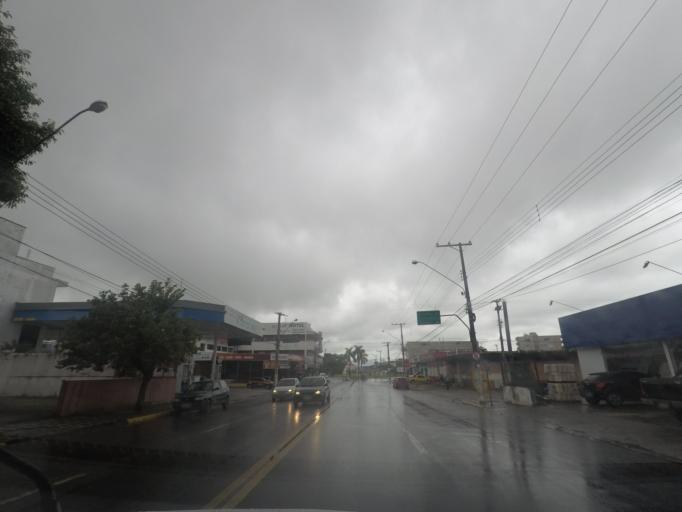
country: BR
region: Sao Paulo
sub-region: Registro
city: Registro
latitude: -24.5008
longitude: -47.8530
